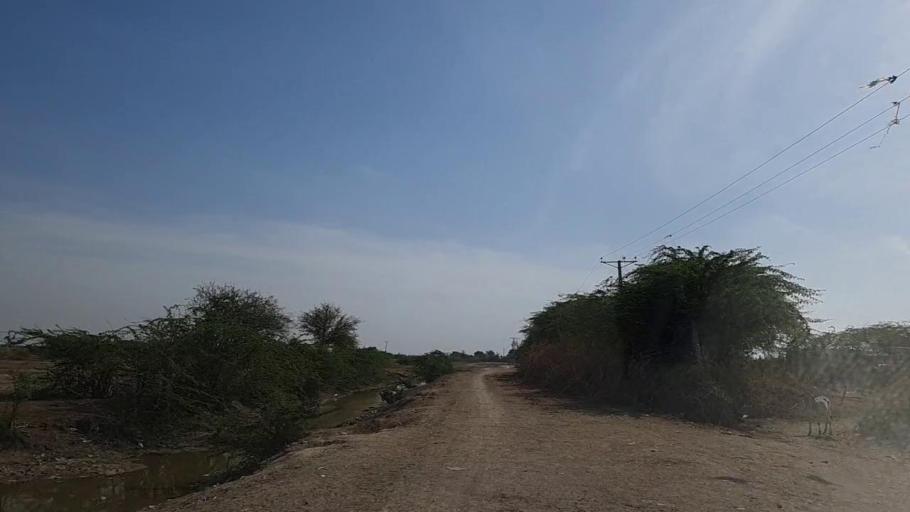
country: PK
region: Sindh
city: Samaro
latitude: 25.2058
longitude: 69.4362
